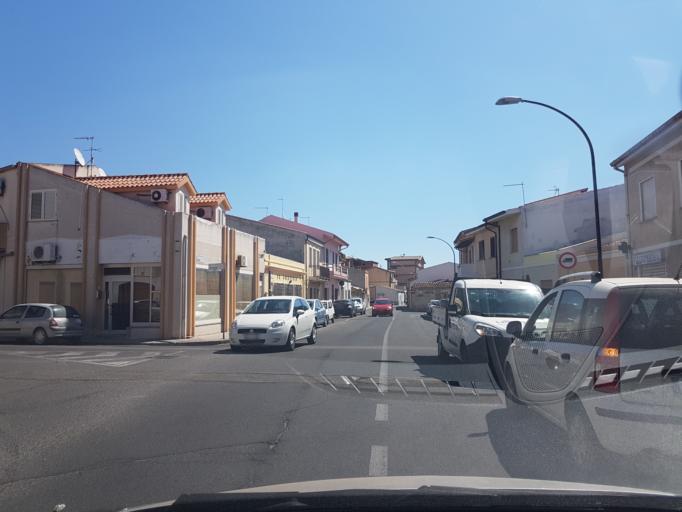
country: IT
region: Sardinia
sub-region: Provincia di Oristano
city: Oristano
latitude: 39.8988
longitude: 8.5949
